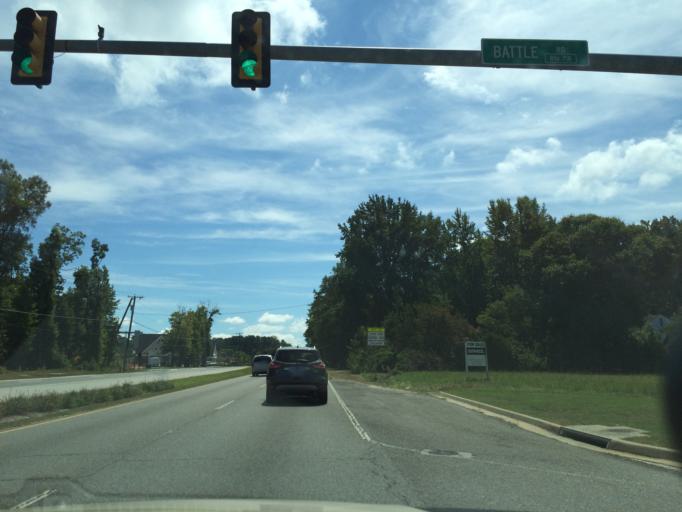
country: US
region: Virginia
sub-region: York County
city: Yorktown
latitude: 37.1944
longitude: -76.4904
